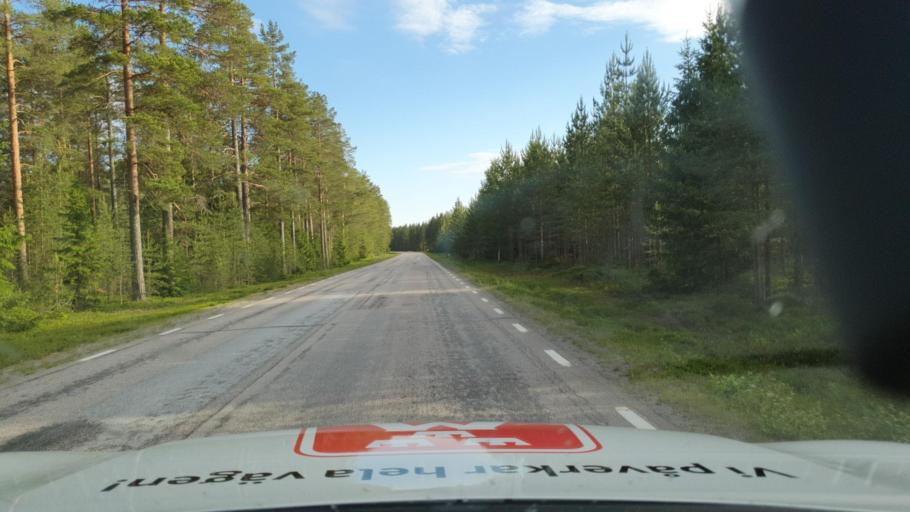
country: SE
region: Vaesterbotten
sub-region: Umea Kommun
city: Roback
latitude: 63.8702
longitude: 20.1482
